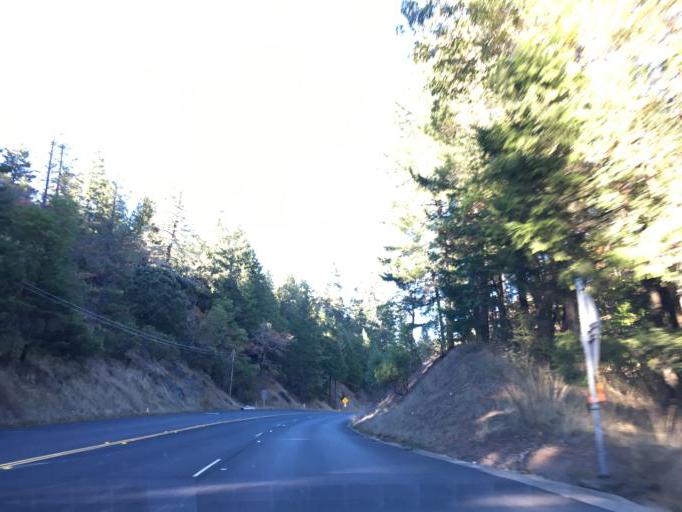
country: US
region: California
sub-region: Mendocino County
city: Laytonville
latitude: 39.7849
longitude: -123.5442
